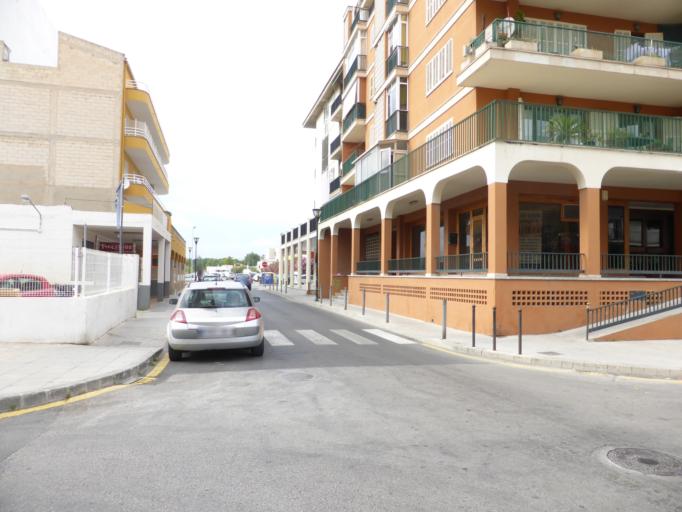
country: ES
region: Balearic Islands
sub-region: Illes Balears
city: Port d'Alcudia
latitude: 39.8436
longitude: 3.1320
